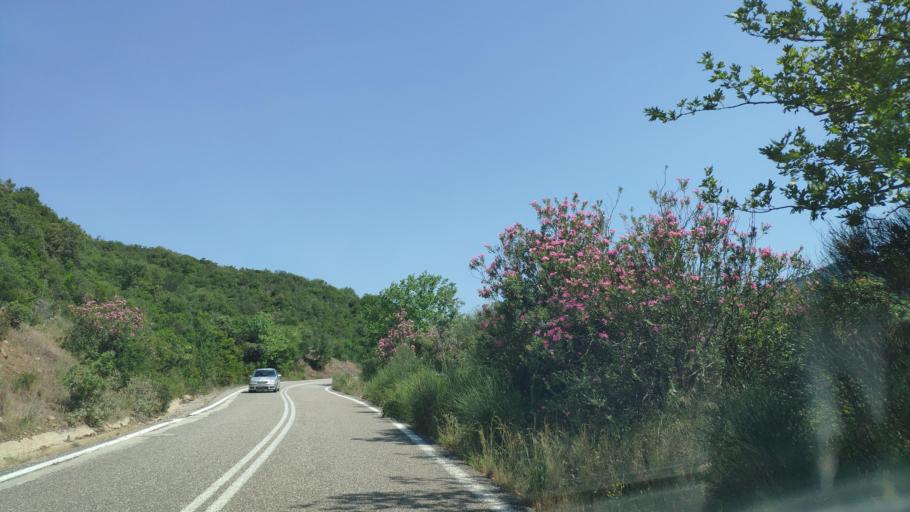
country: GR
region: West Greece
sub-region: Nomos Aitolias kai Akarnanias
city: Lepenou
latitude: 38.7645
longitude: 21.3374
